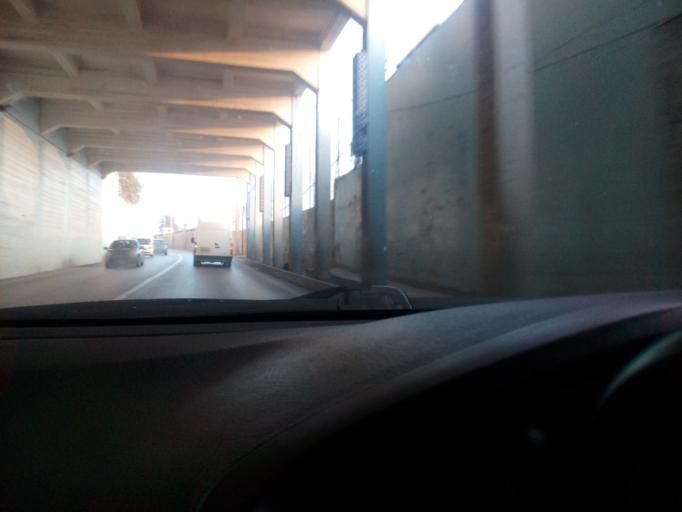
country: DZ
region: Oran
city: Oran
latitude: 35.7107
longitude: -0.6569
